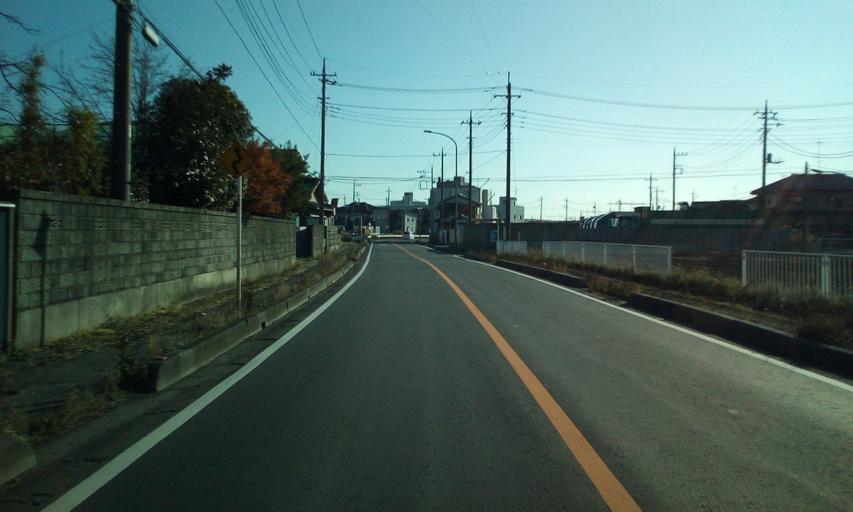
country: JP
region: Chiba
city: Nagareyama
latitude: 35.8652
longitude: 139.8882
